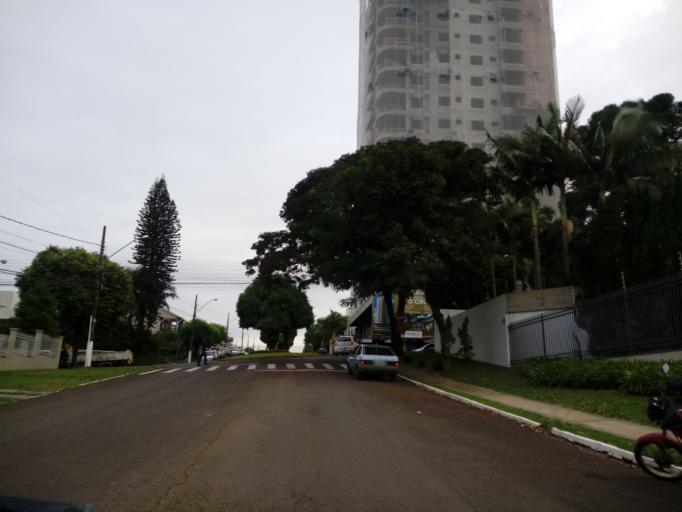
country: BR
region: Santa Catarina
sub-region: Chapeco
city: Chapeco
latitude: -27.0937
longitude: -52.6077
